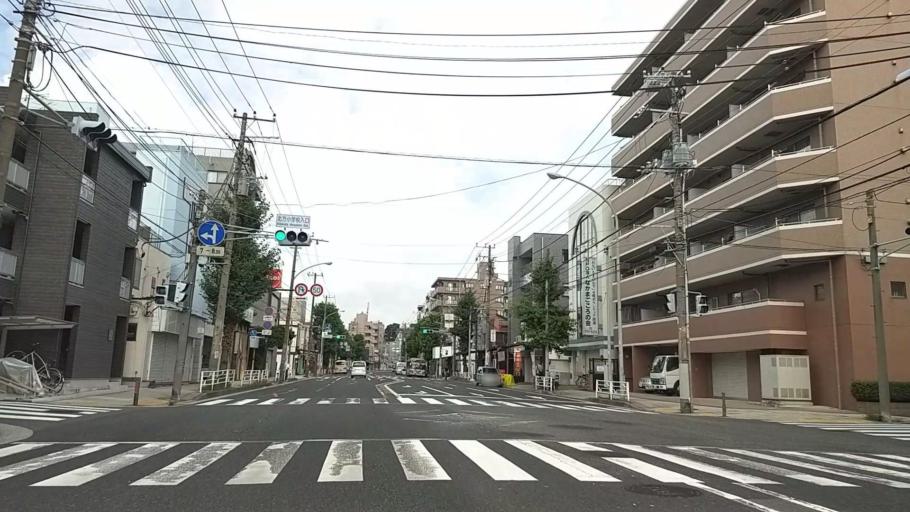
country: JP
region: Kanagawa
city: Yokohama
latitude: 35.4323
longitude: 139.6529
